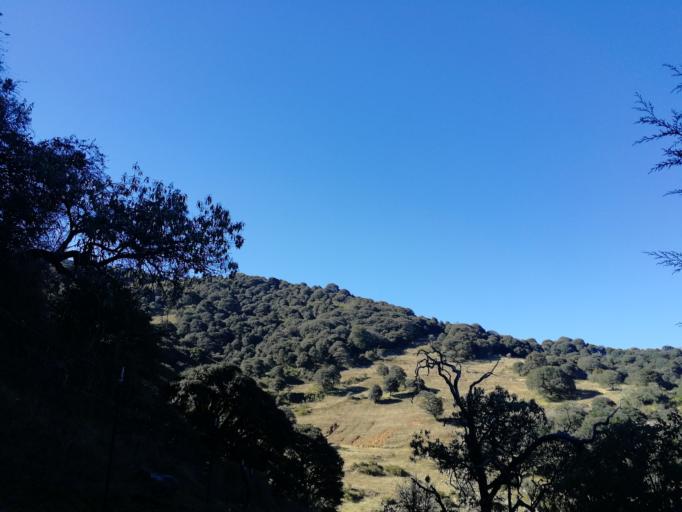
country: MX
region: San Luis Potosi
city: Zaragoza
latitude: 22.0155
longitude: -100.6101
